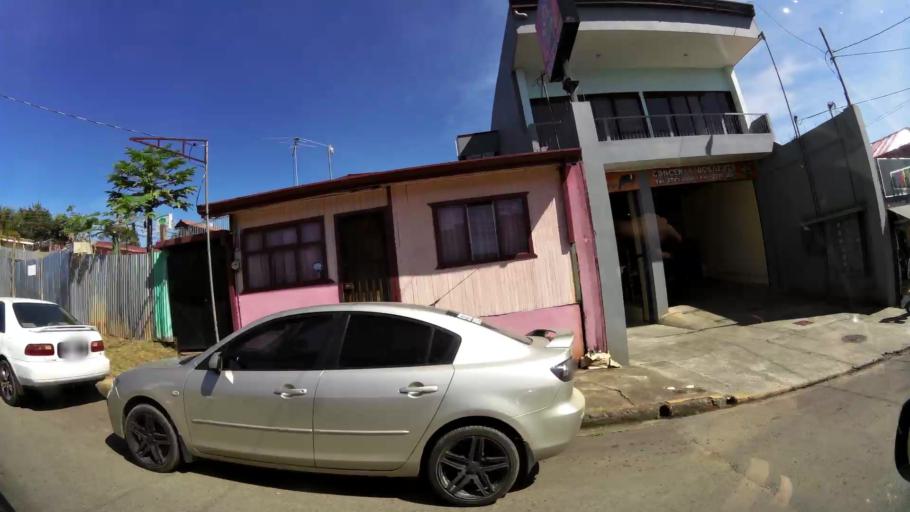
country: CR
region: San Jose
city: San Isidro
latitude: 9.3738
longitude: -83.7061
